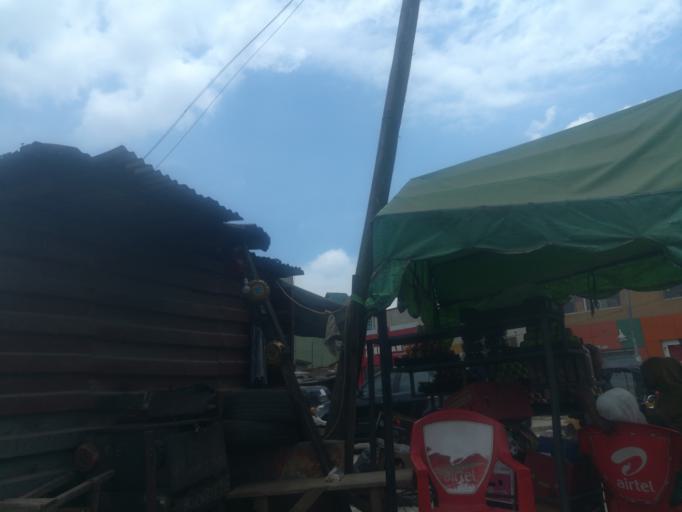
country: NG
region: Lagos
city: Somolu
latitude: 6.5537
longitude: 3.3905
